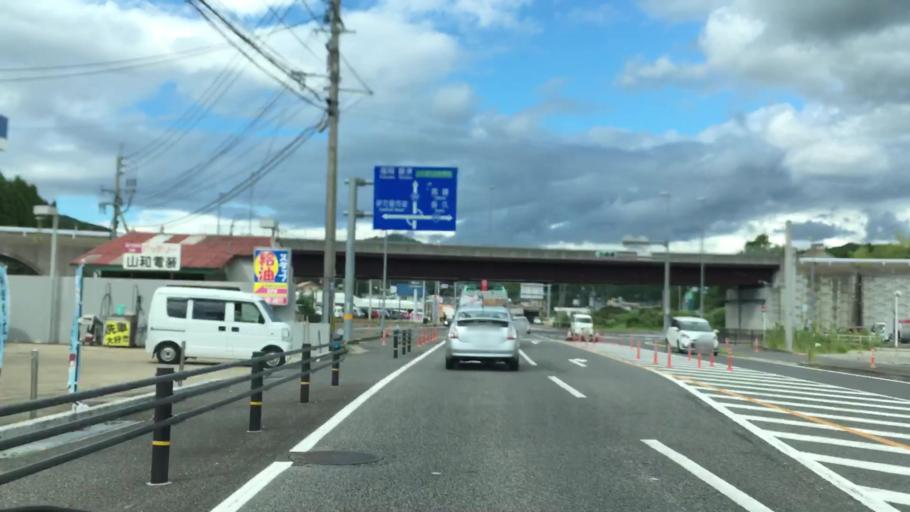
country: JP
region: Saga Prefecture
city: Imaricho-ko
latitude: 33.2809
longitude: 129.8962
